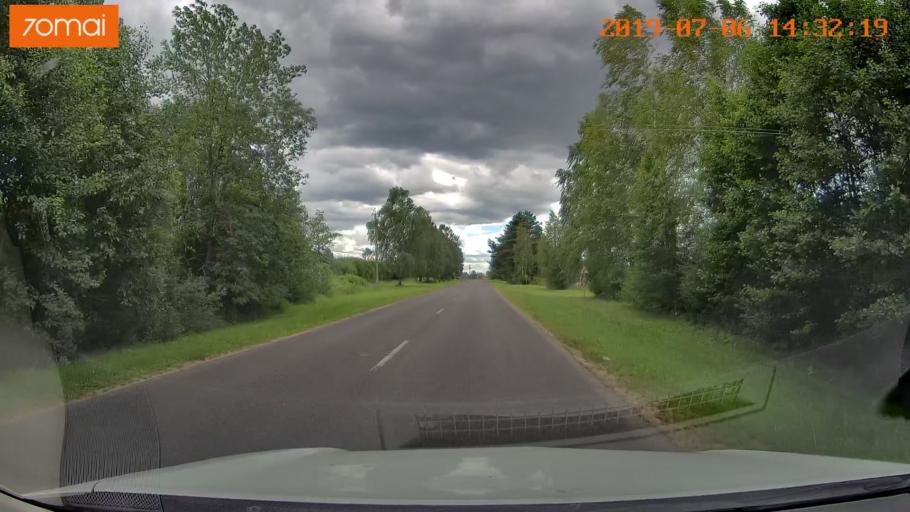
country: BY
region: Minsk
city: Ivyanyets
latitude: 53.9082
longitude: 26.7631
